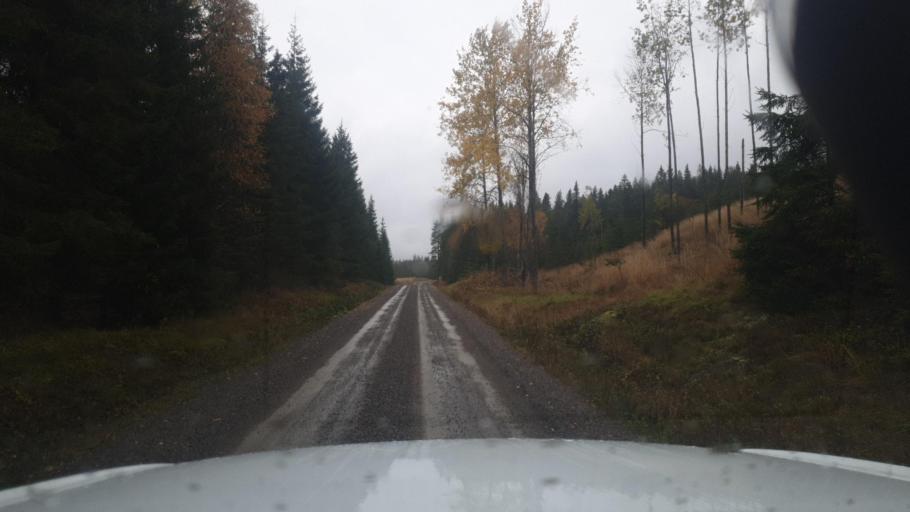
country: SE
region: Vaermland
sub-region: Eda Kommun
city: Charlottenberg
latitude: 60.0444
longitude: 12.6307
